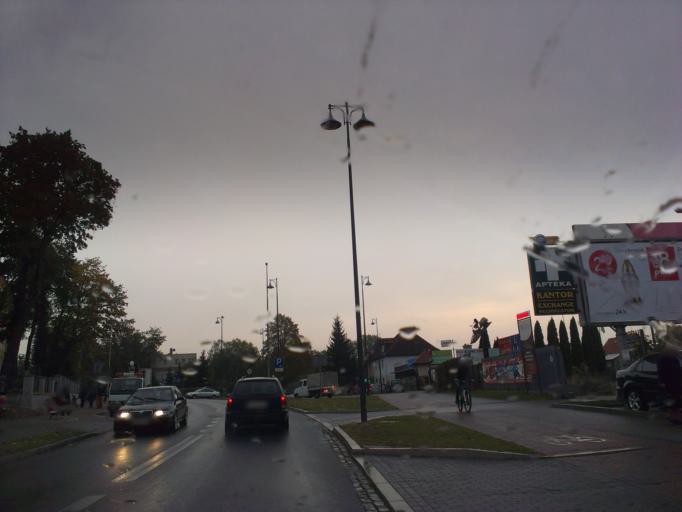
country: PL
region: West Pomeranian Voivodeship
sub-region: Powiat szczecinecki
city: Szczecinek
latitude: 53.7031
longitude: 16.6987
